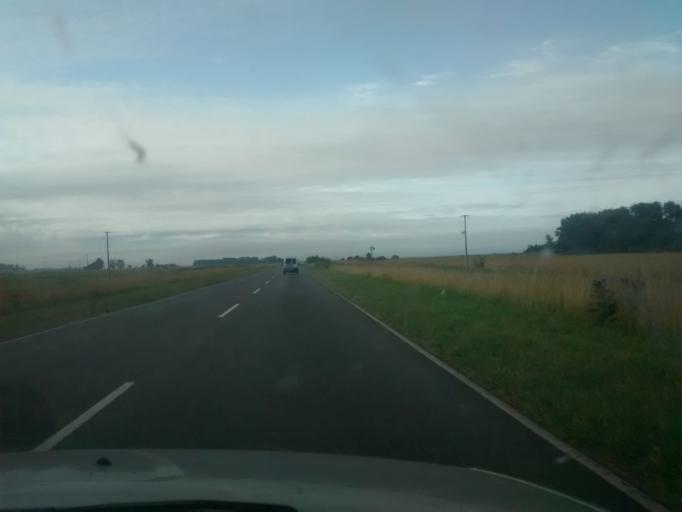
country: AR
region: Buenos Aires
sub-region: Partido de Brandsen
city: Brandsen
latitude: -35.3177
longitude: -58.2402
